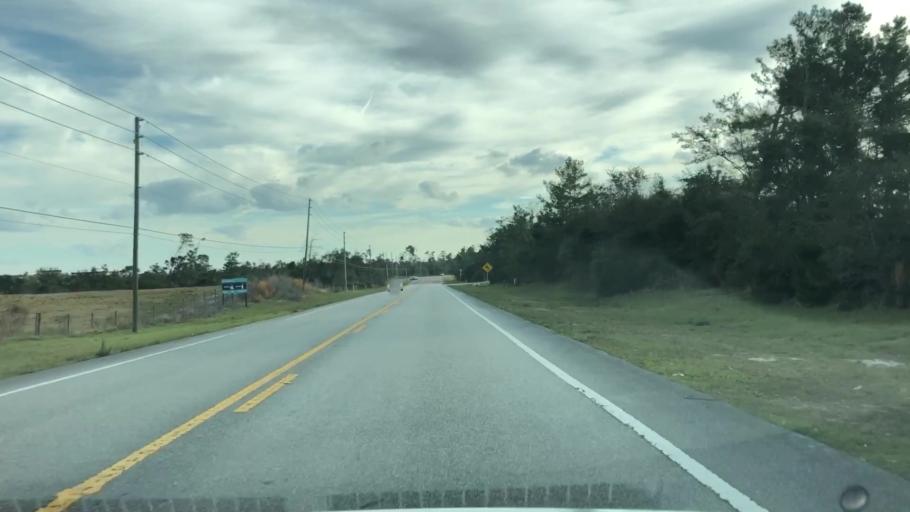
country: US
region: Florida
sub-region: Volusia County
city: Lake Helen
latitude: 28.9466
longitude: -81.2554
